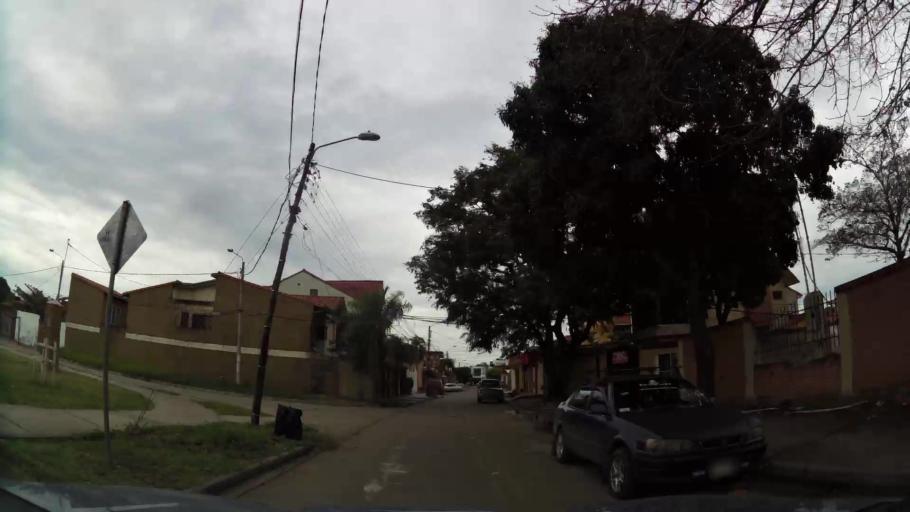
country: BO
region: Santa Cruz
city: Santa Cruz de la Sierra
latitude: -17.7790
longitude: -63.1579
